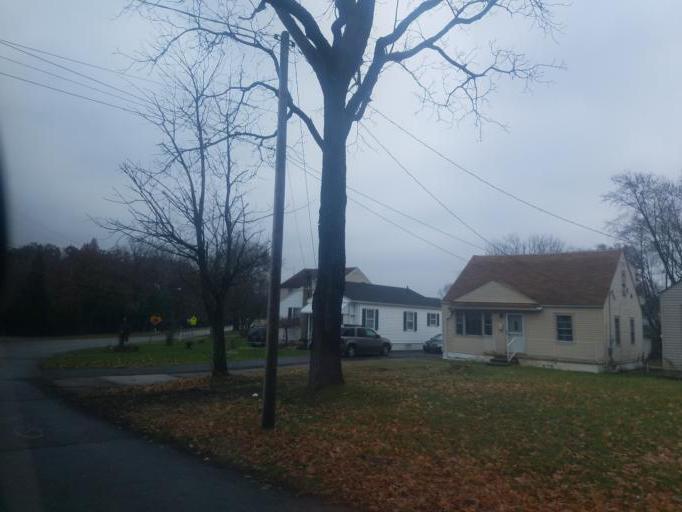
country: US
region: Ohio
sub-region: Richland County
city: Mansfield
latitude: 40.7605
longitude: -82.5470
